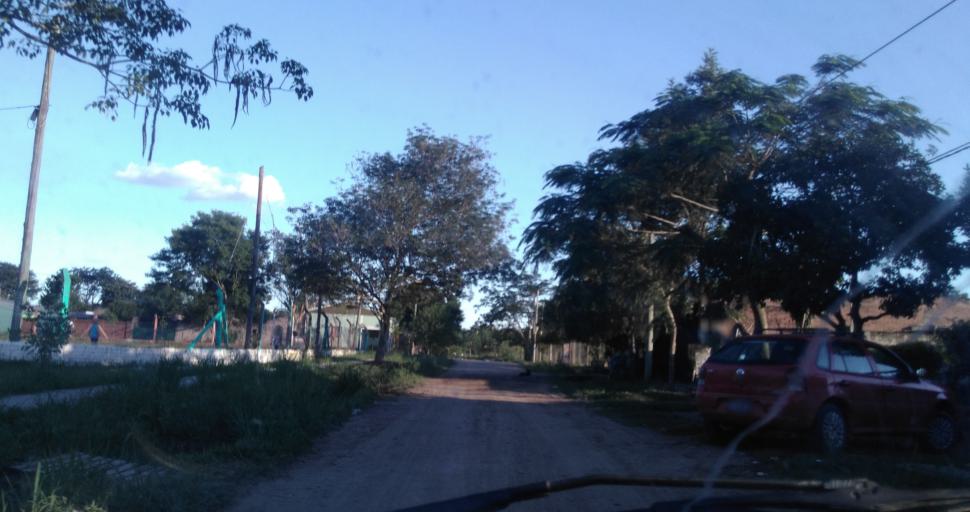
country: AR
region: Chaco
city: Resistencia
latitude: -27.4379
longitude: -58.9613
